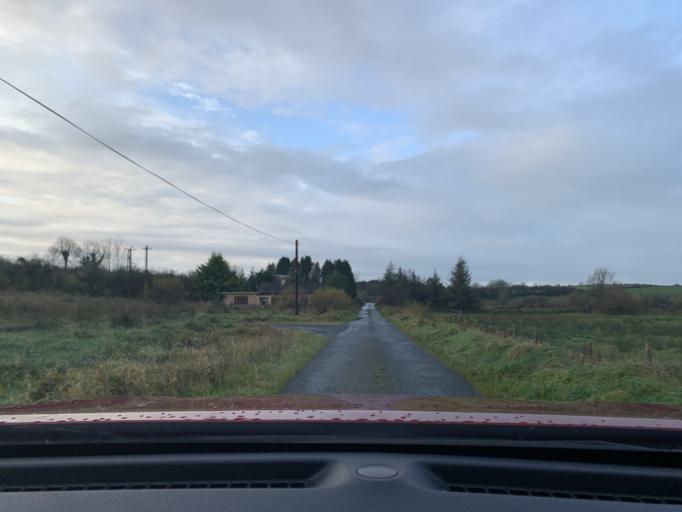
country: IE
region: Connaught
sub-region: Sligo
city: Ballymote
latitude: 54.0444
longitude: -8.5493
